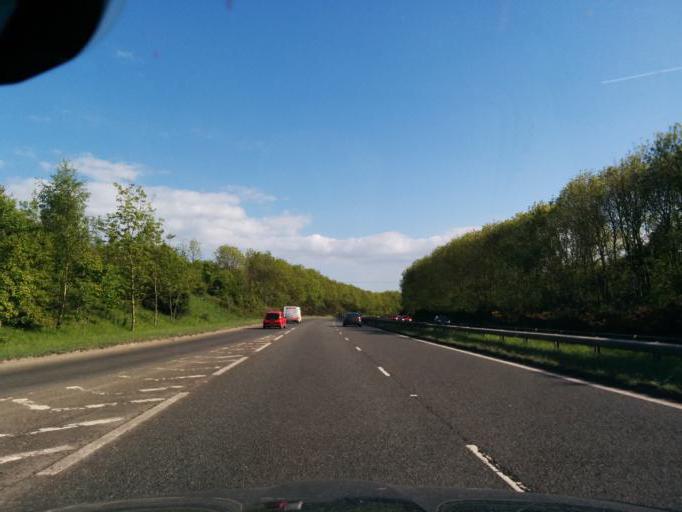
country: GB
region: England
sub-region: Northumberland
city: Bedlington
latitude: 55.1255
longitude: -1.5558
